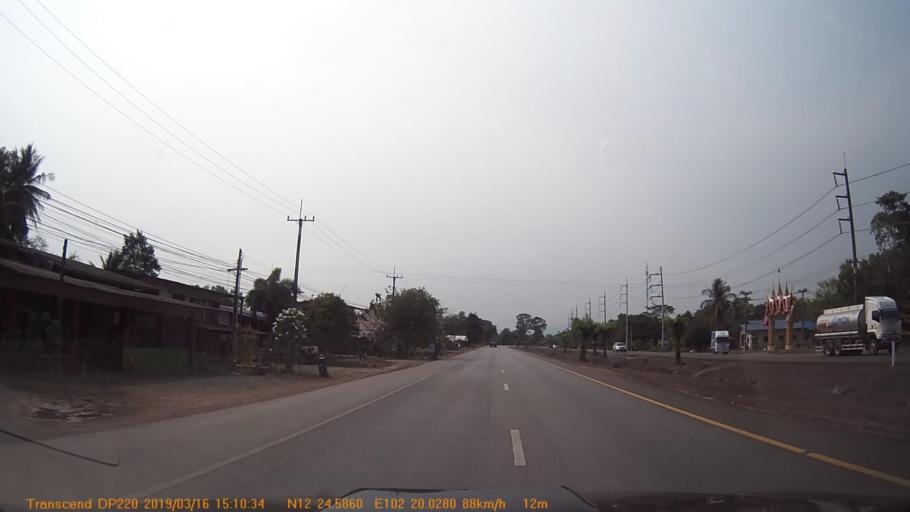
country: TH
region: Trat
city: Khao Saming
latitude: 12.4100
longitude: 102.3335
